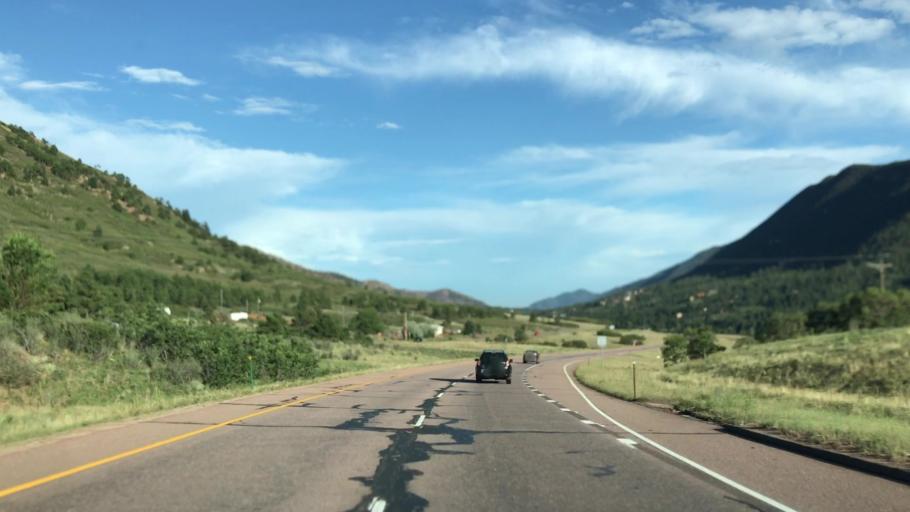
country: US
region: Colorado
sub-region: El Paso County
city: Cascade-Chipita Park
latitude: 38.9313
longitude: -105.0013
